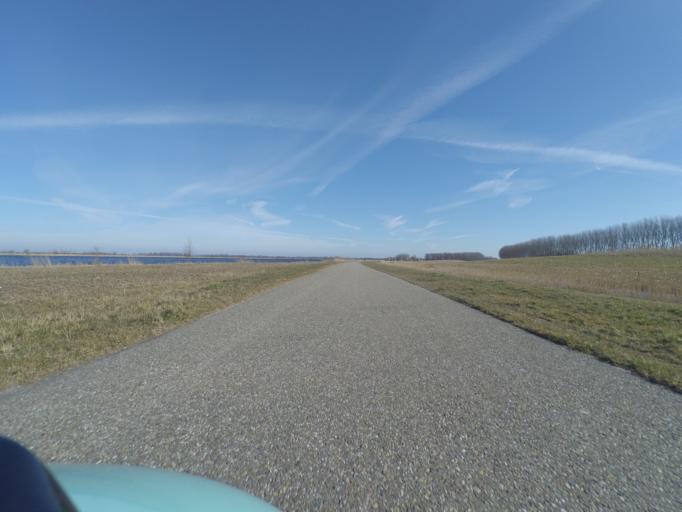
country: NL
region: Flevoland
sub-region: Gemeente Almere
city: Almere Stad
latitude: 52.3864
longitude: 5.1888
